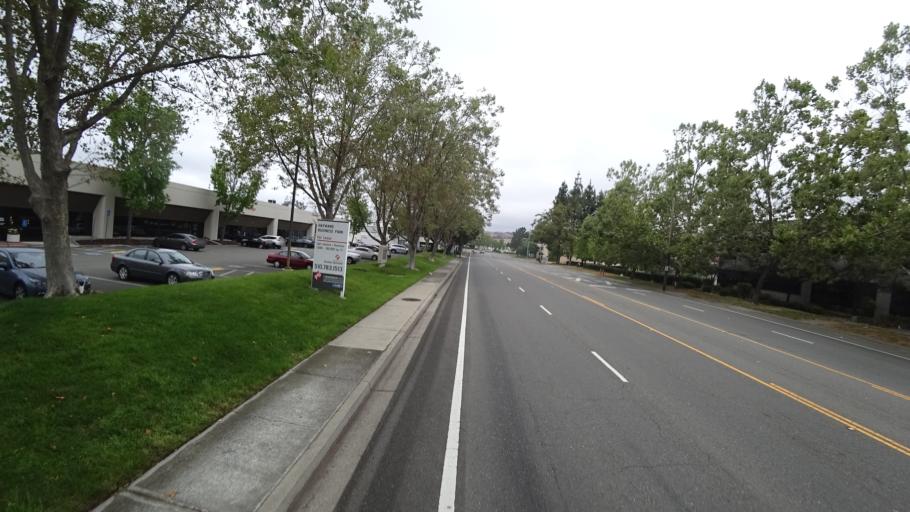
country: US
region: California
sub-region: Alameda County
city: Union City
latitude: 37.6175
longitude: -122.0549
